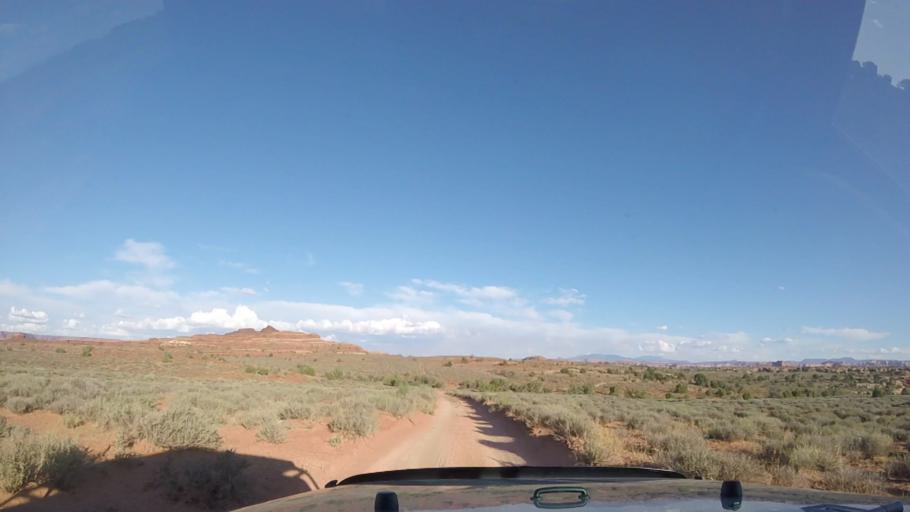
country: US
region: Utah
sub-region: Grand County
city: Moab
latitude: 38.2123
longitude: -109.7890
